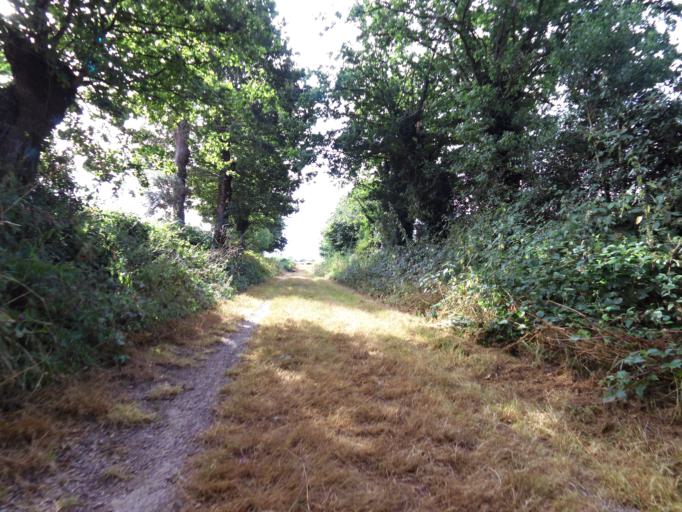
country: FR
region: Brittany
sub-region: Departement d'Ille-et-Vilaine
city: Chanteloup
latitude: 47.9302
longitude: -1.6023
